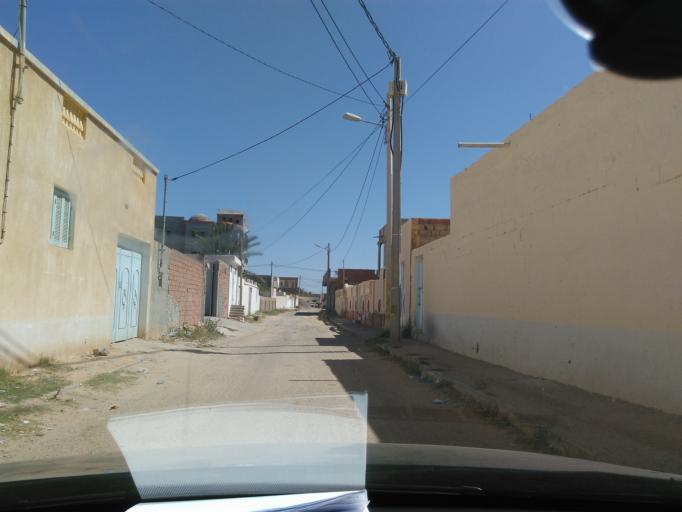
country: TN
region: Tataouine
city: Tataouine
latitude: 32.9512
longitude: 10.4676
